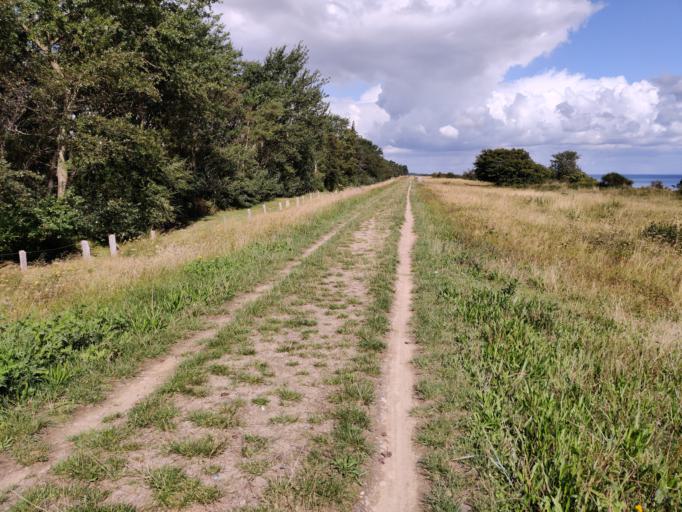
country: DK
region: Zealand
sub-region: Guldborgsund Kommune
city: Nykobing Falster
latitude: 54.5923
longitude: 11.9699
